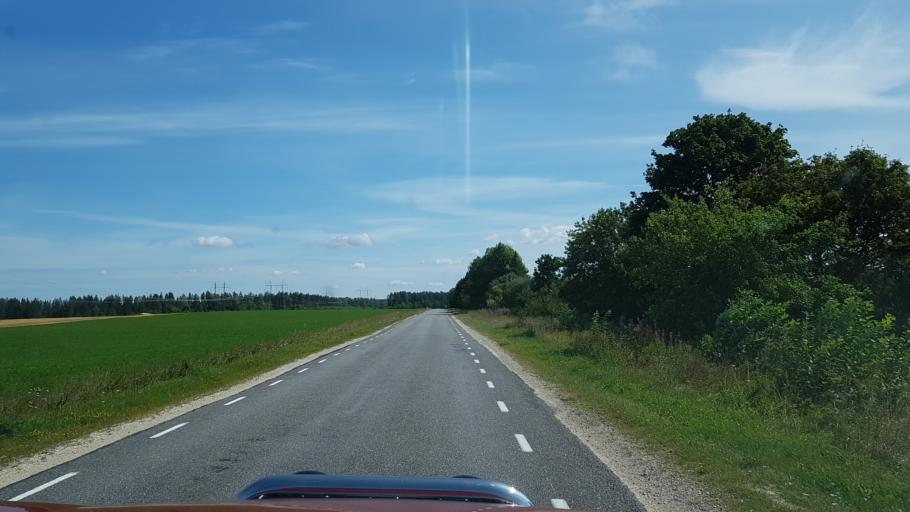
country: EE
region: Laeaene-Virumaa
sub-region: Tapa vald
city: Tapa
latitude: 59.1812
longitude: 25.9568
